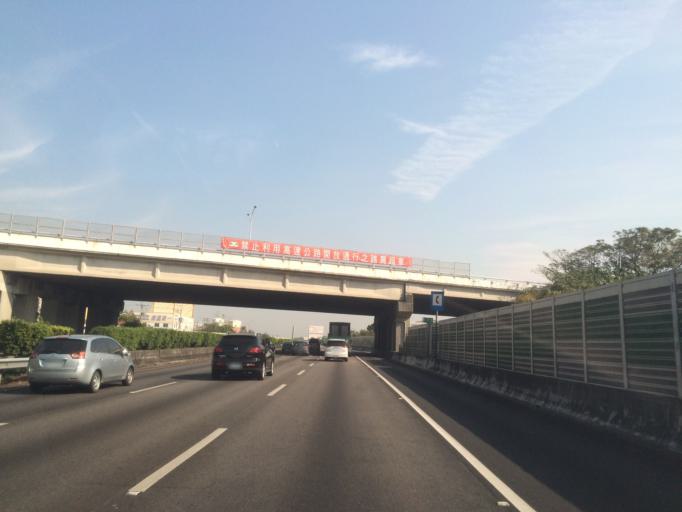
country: TW
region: Taiwan
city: Fengyuan
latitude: 24.2156
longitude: 120.6752
